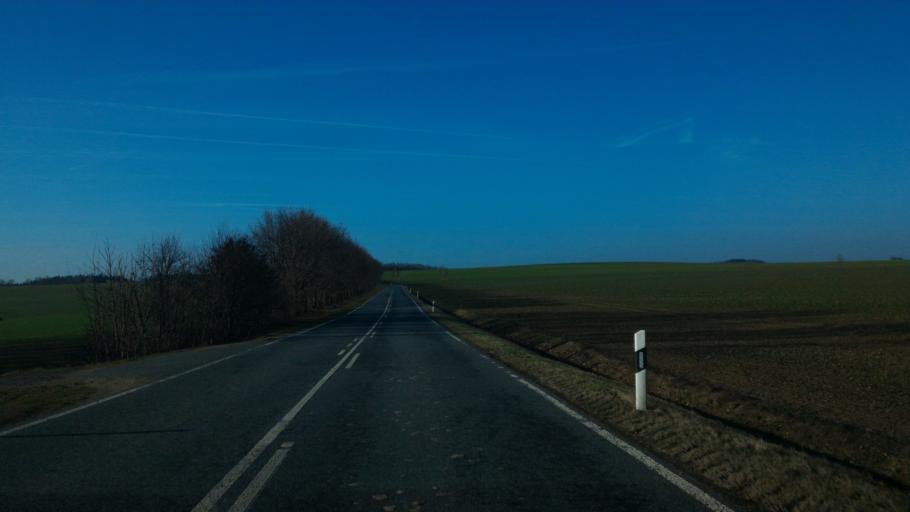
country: DE
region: Saxony
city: Stolpen
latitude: 51.0355
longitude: 14.1346
